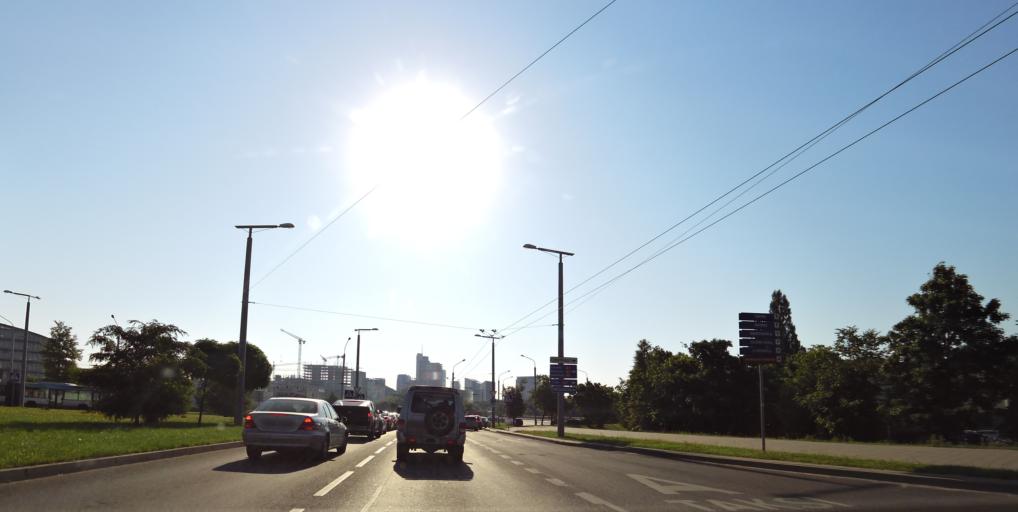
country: LT
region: Vilnius County
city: Seskine
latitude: 54.6983
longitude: 25.2616
